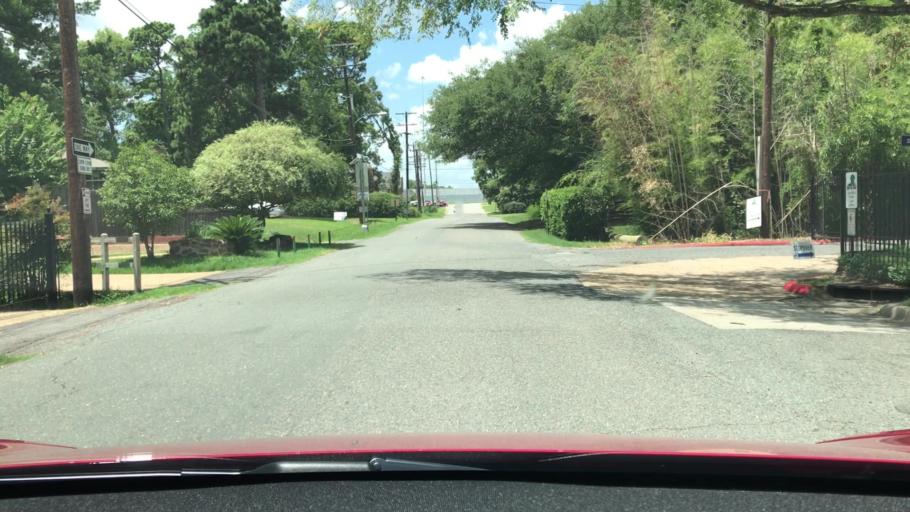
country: US
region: Louisiana
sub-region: Bossier Parish
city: Bossier City
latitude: 32.4565
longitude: -93.7527
